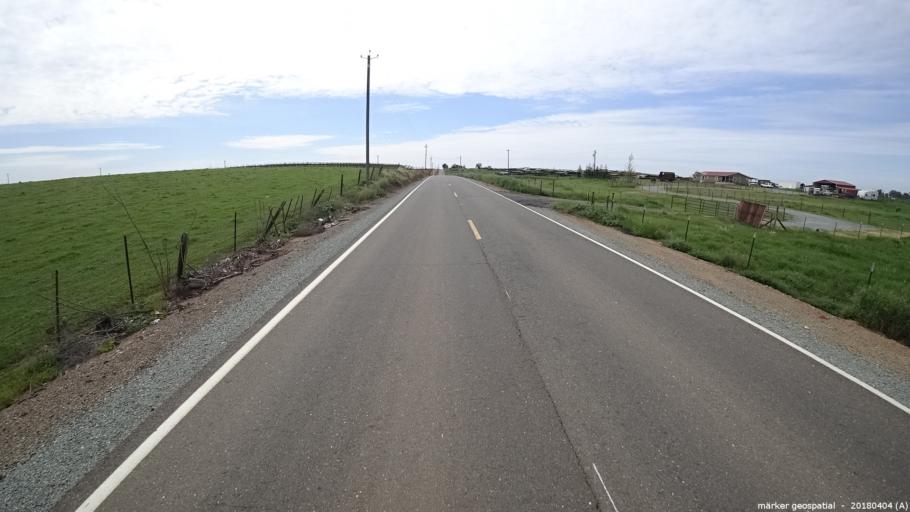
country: US
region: California
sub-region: Sacramento County
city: Clay
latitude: 38.2872
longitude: -121.1713
